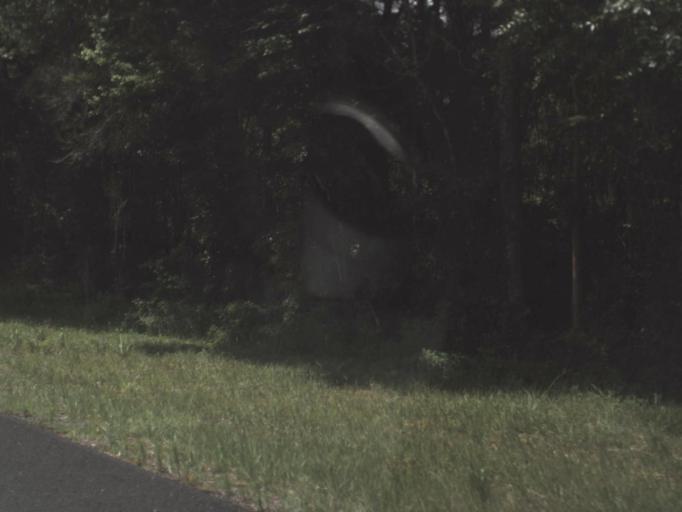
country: US
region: Florida
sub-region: Taylor County
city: Perry
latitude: 30.1877
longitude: -83.6437
